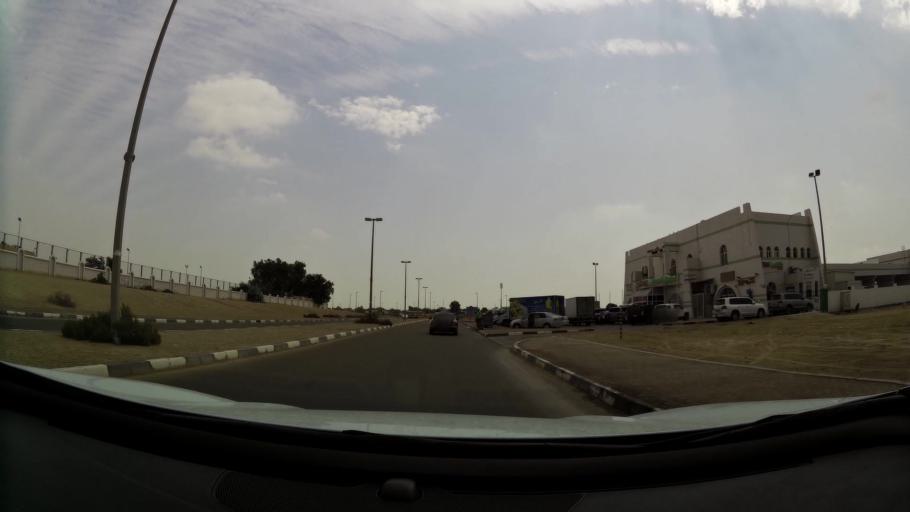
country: AE
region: Abu Dhabi
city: Abu Dhabi
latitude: 24.5252
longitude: 54.6768
